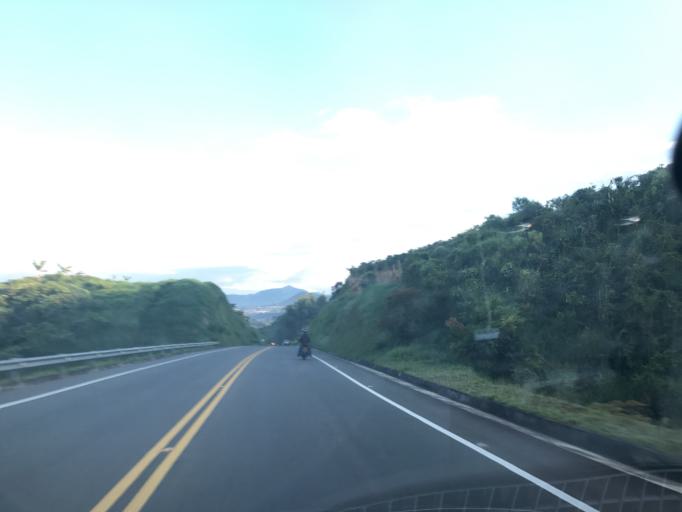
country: CO
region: Risaralda
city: Pereira
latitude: 4.7717
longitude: -75.7106
